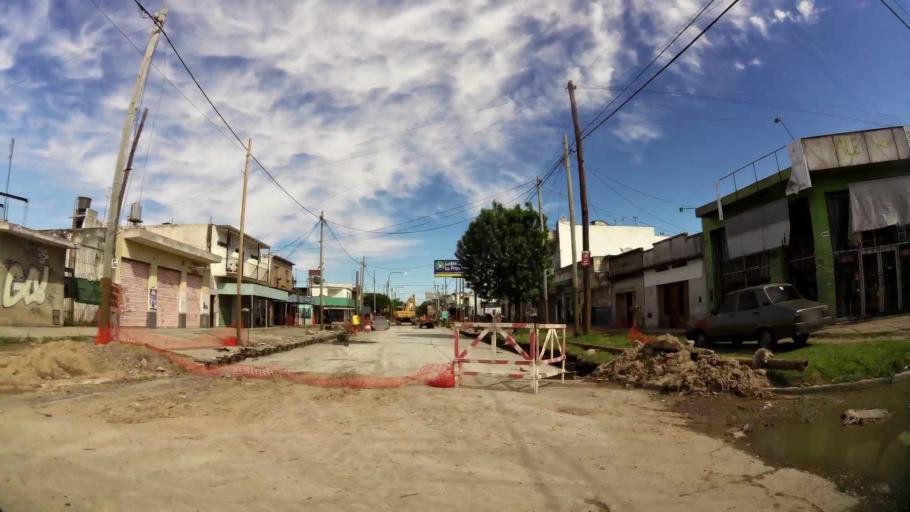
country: AR
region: Buenos Aires
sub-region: Partido de Quilmes
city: Quilmes
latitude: -34.7833
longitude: -58.3032
